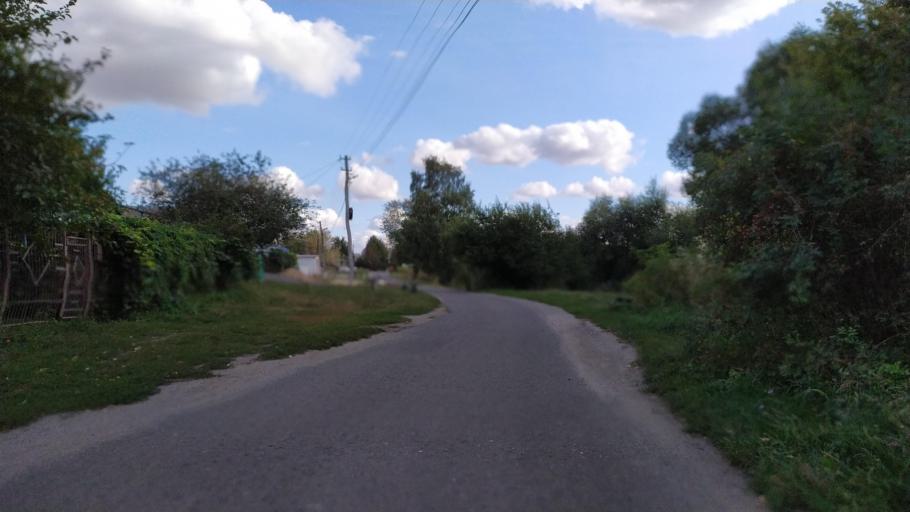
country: RU
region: Kursk
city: Kursk
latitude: 51.6310
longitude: 36.1528
